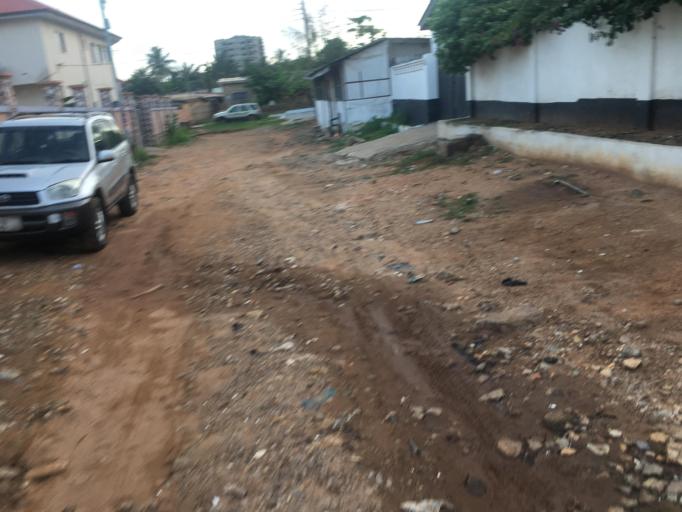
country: GH
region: Greater Accra
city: Gbawe
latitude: 5.5681
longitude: -0.2547
